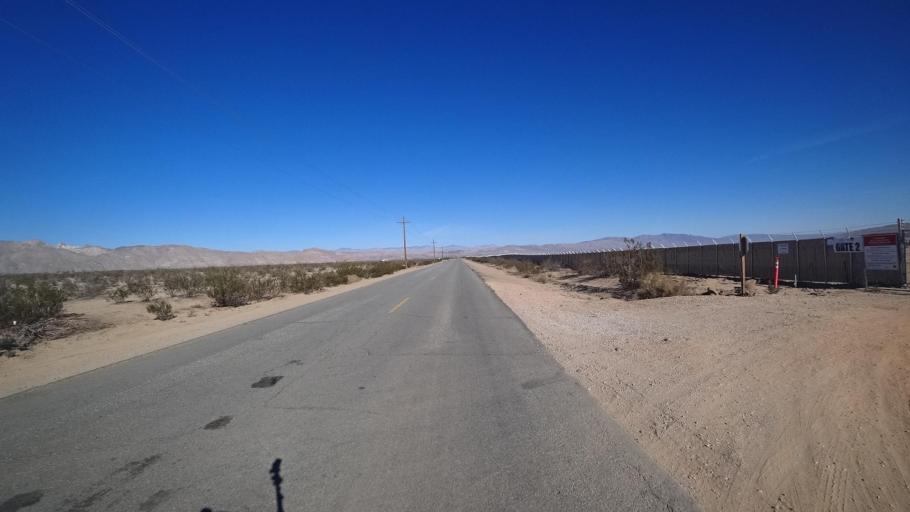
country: US
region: California
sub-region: Kern County
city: California City
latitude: 35.2150
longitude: -117.9858
